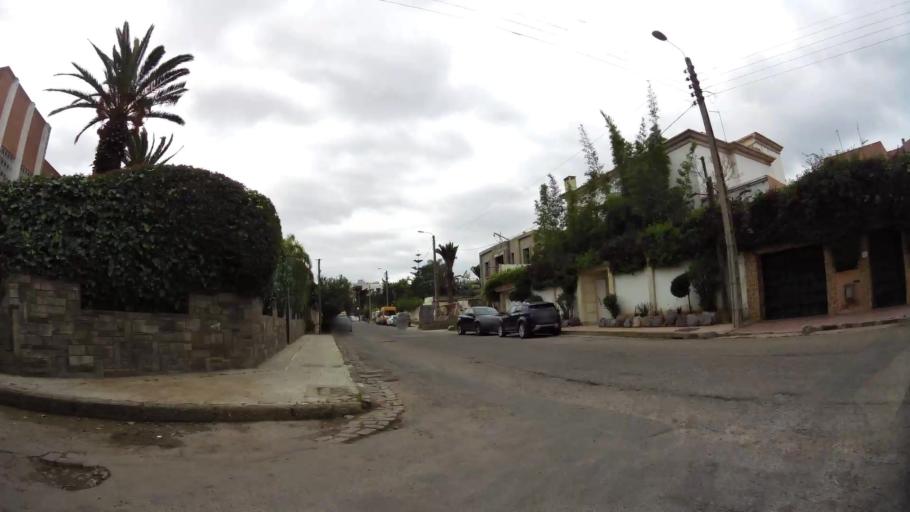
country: MA
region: Grand Casablanca
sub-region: Casablanca
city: Casablanca
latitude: 33.5594
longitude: -7.6311
